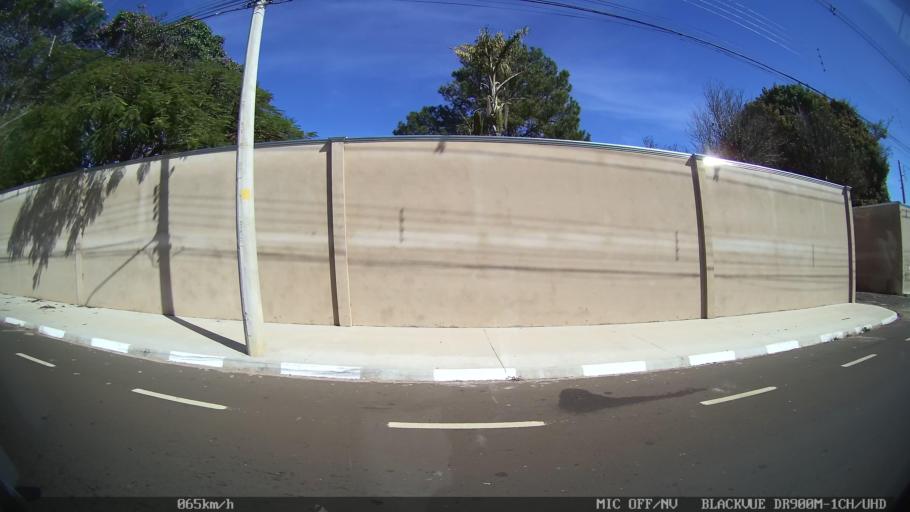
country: BR
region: Sao Paulo
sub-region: Franca
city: Franca
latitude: -20.5595
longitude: -47.3594
